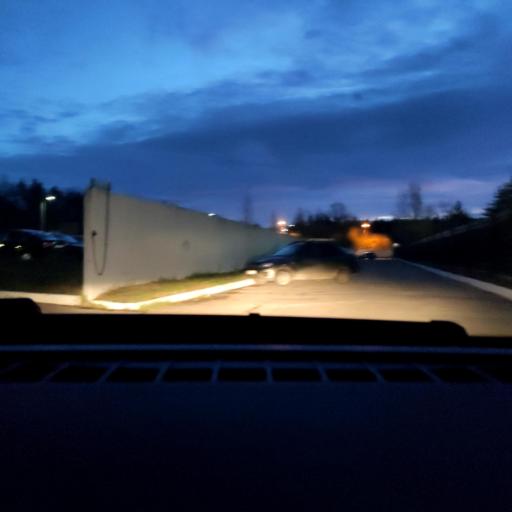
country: RU
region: Voronezj
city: Somovo
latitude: 51.7408
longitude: 39.3011
